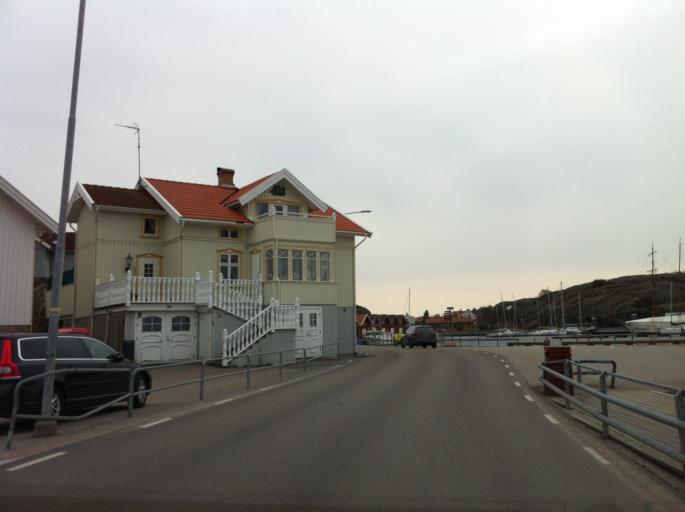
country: SE
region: Vaestra Goetaland
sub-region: Orust
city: Henan
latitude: 58.1595
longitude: 11.7059
